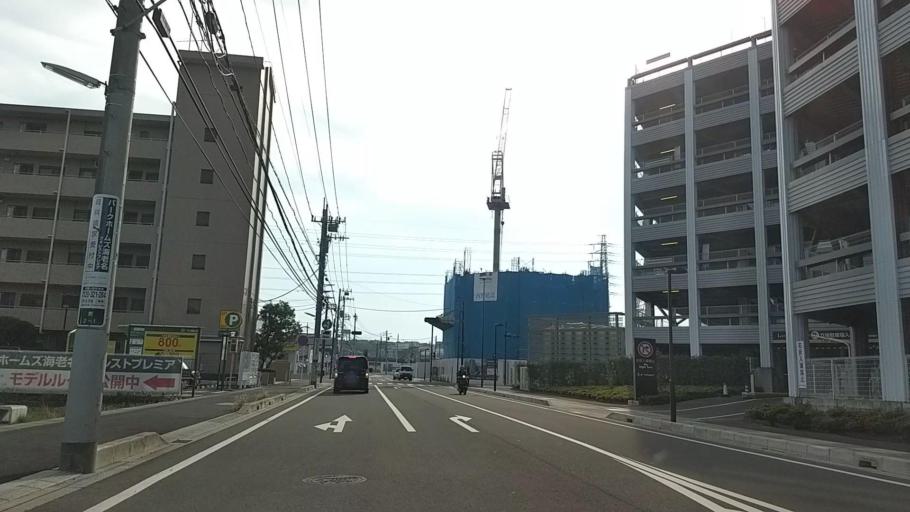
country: JP
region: Kanagawa
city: Zama
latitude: 35.4572
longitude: 139.3896
